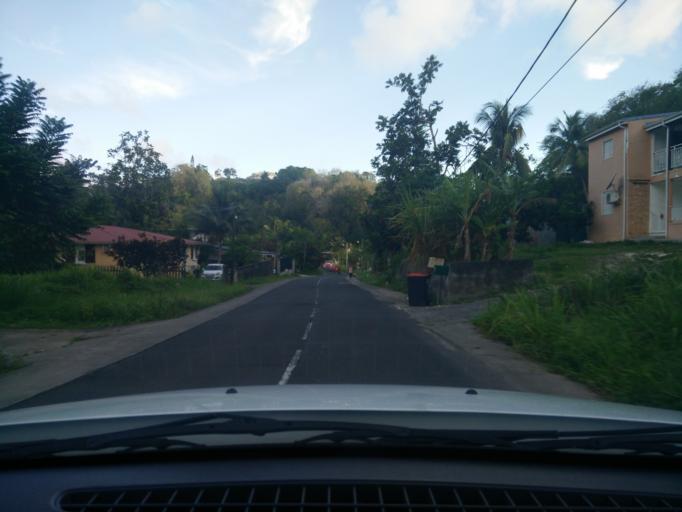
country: GP
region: Guadeloupe
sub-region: Guadeloupe
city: Les Abymes
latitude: 16.2434
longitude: -61.4926
